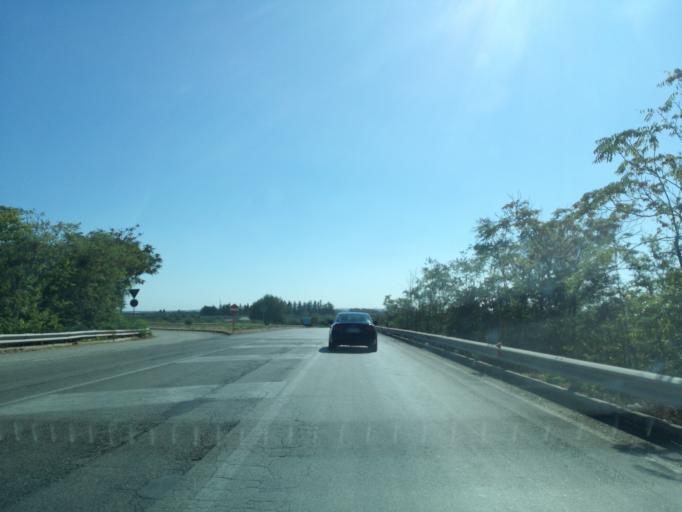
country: IT
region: Apulia
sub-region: Provincia di Bari
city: Casamassima
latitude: 40.9490
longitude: 16.9327
